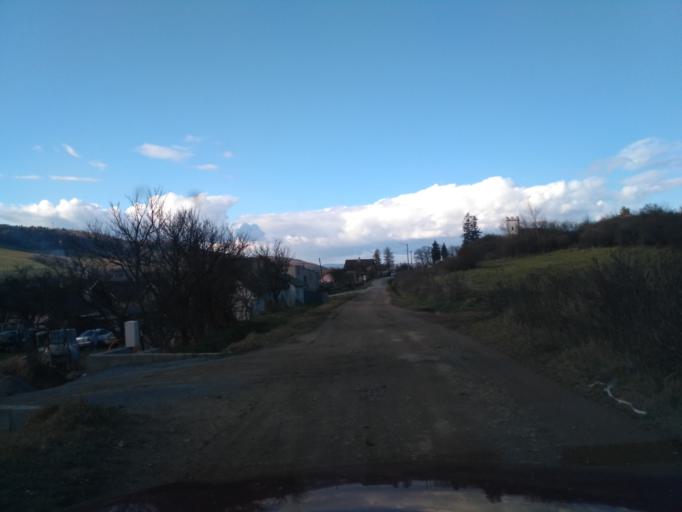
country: SK
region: Presovsky
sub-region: Okres Presov
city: Presov
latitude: 48.9305
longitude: 21.1936
